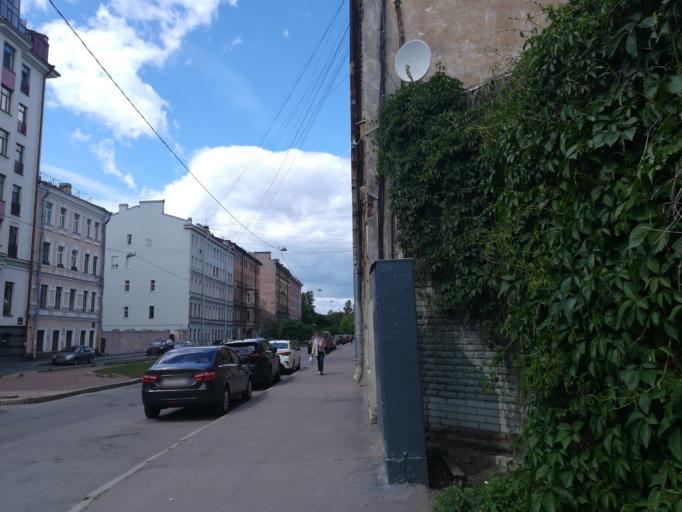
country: RU
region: St.-Petersburg
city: Vasyl'evsky Ostrov
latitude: 59.9456
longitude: 30.2627
